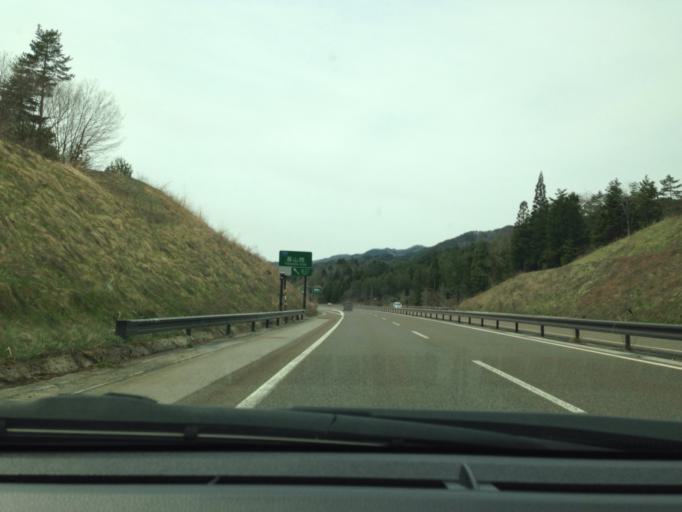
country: JP
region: Gifu
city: Takayama
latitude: 36.1386
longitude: 137.1757
